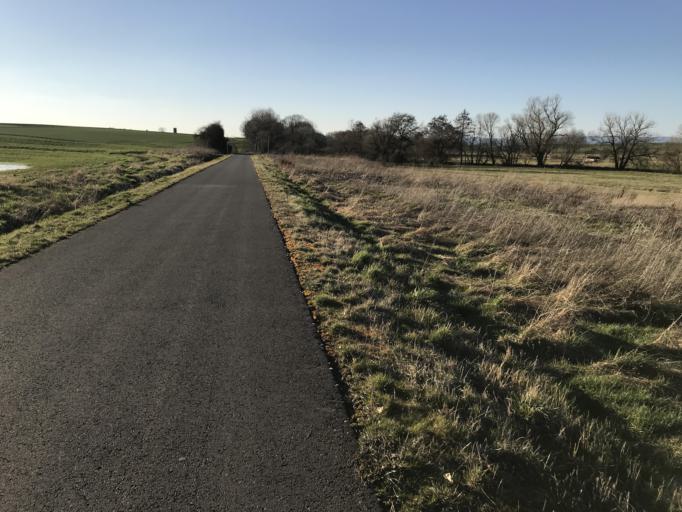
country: DE
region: Hesse
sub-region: Regierungsbezirk Kassel
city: Schrecksbach
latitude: 50.8733
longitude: 9.2854
